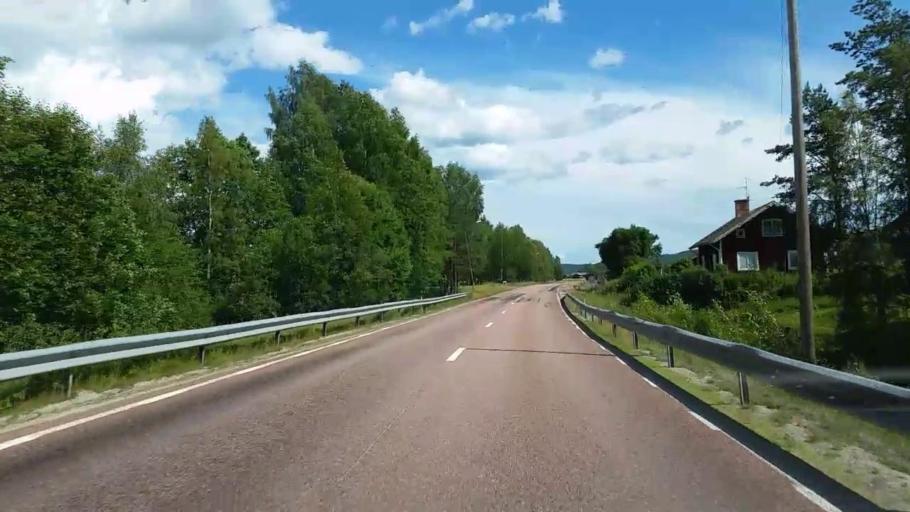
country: SE
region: Gaevleborg
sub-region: Ovanakers Kommun
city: Edsbyn
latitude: 61.3468
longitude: 15.6153
